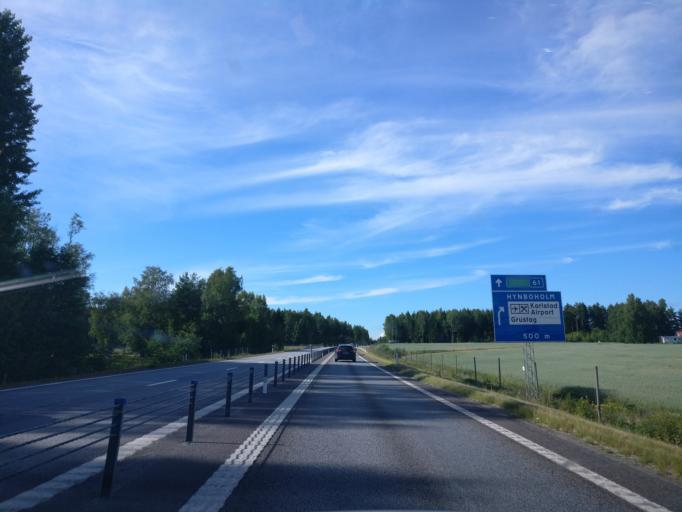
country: SE
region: Vaermland
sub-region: Kils Kommun
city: Kil
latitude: 59.4505
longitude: 13.3758
